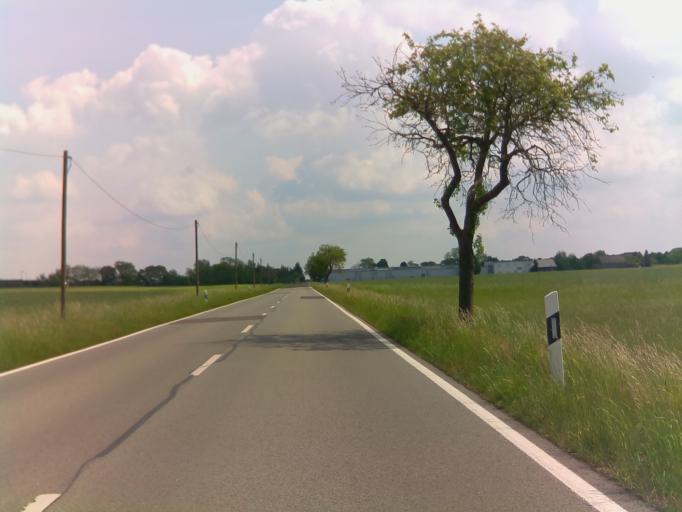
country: DE
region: Brandenburg
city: Kotzen
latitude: 52.6170
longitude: 12.5898
